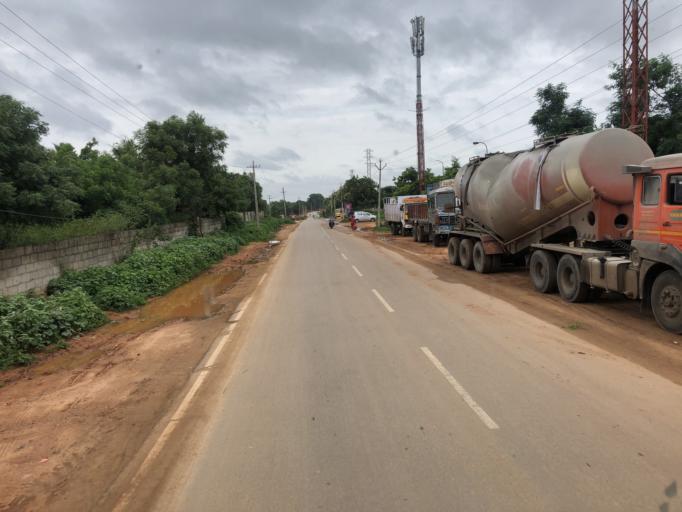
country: IN
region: Telangana
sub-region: Medak
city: Serilingampalle
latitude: 17.4349
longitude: 78.2993
